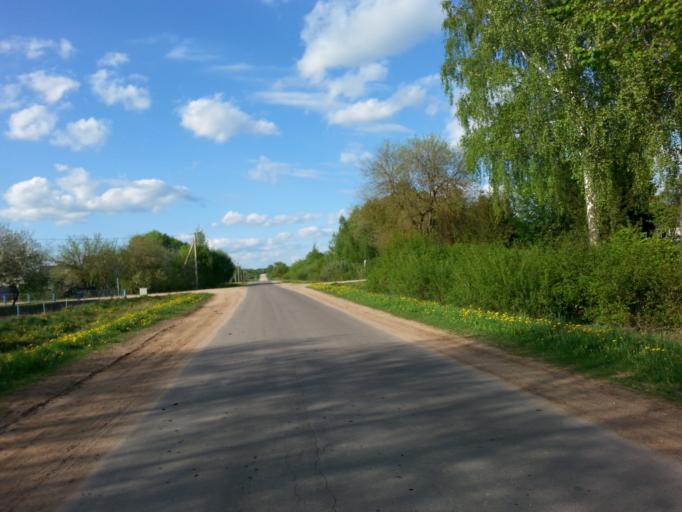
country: BY
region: Minsk
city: Narach
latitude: 54.9423
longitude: 26.6935
